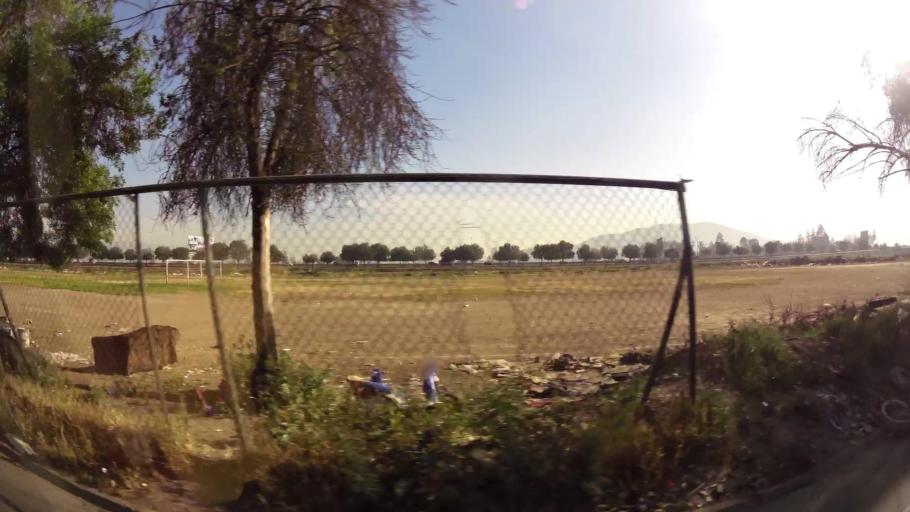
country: CL
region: Santiago Metropolitan
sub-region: Provincia de Santiago
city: Lo Prado
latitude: -33.4134
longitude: -70.7510
